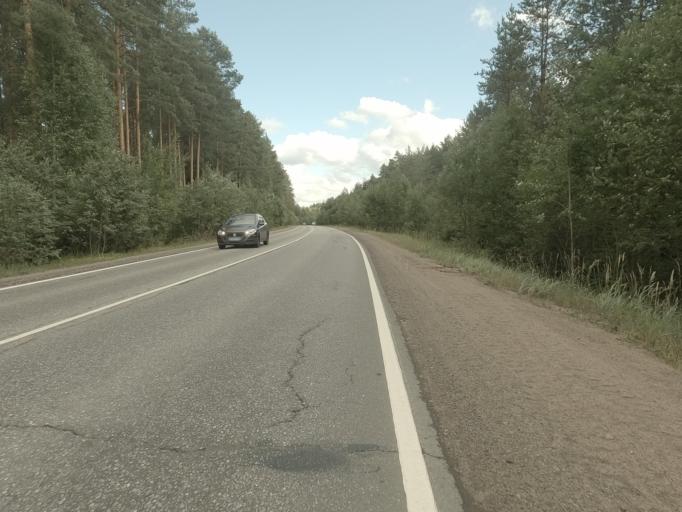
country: RU
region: Leningrad
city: Shcheglovo
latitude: 60.0099
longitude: 30.8569
